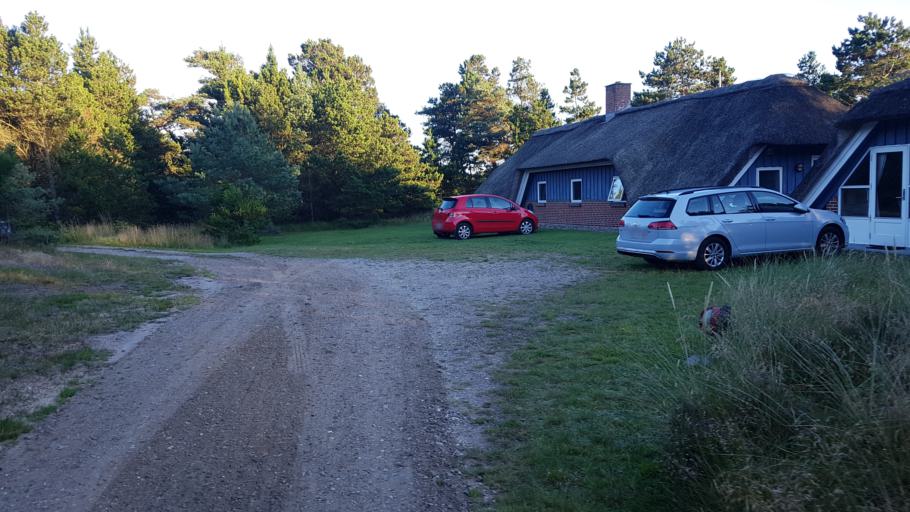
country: DE
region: Schleswig-Holstein
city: List
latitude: 55.0996
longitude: 8.5393
